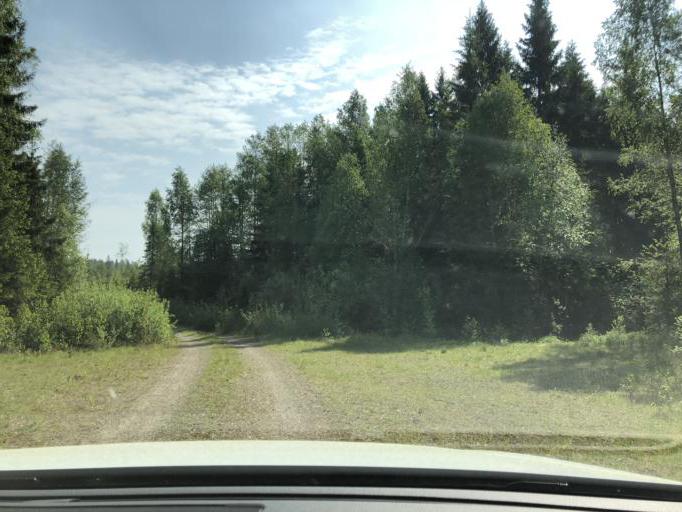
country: SE
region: Dalarna
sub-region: Avesta Kommun
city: Horndal
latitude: 60.2163
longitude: 16.5169
